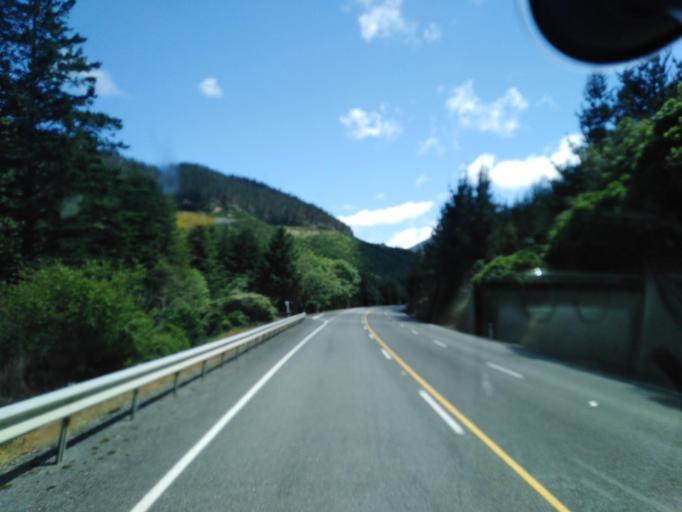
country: NZ
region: Nelson
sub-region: Nelson City
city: Nelson
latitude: -41.1817
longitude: 173.5595
